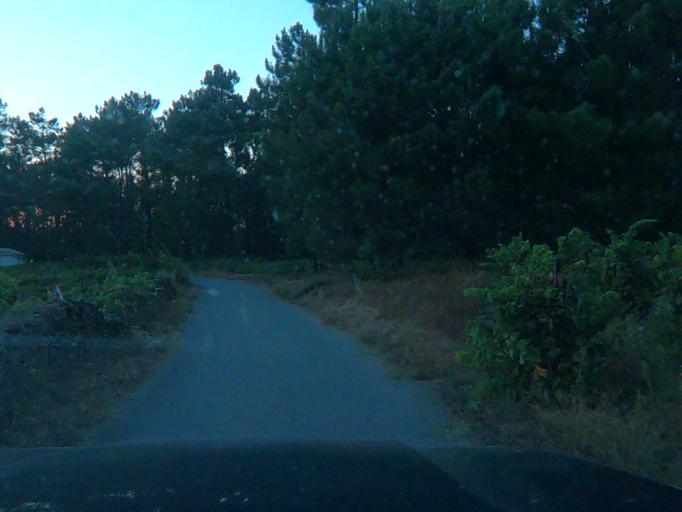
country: PT
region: Vila Real
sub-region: Sabrosa
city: Vilela
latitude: 41.2452
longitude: -7.6262
